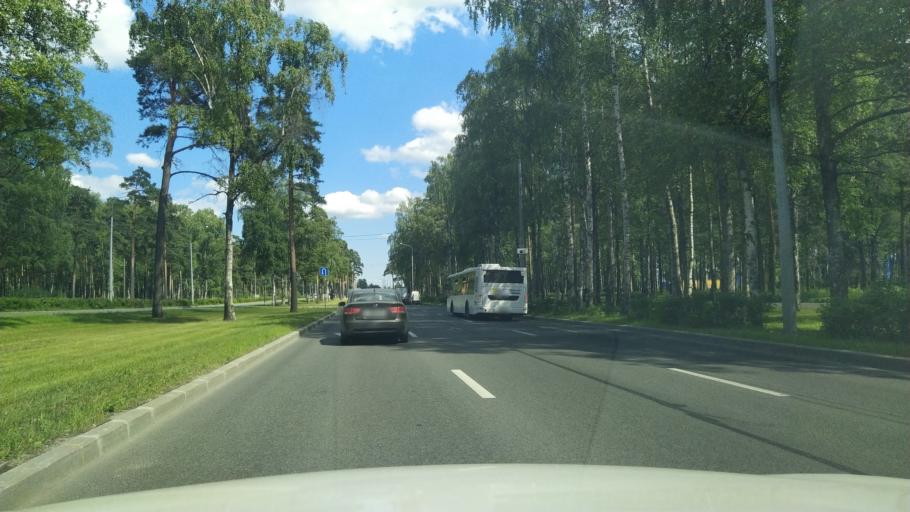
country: RU
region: Leningrad
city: Kalininskiy
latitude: 59.9947
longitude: 30.3981
